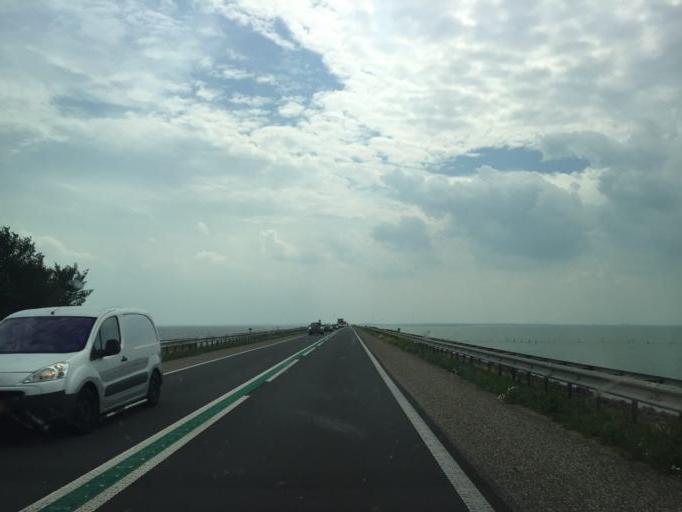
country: NL
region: Flevoland
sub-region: Gemeente Lelystad
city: Lelystad
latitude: 52.6341
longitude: 5.4146
